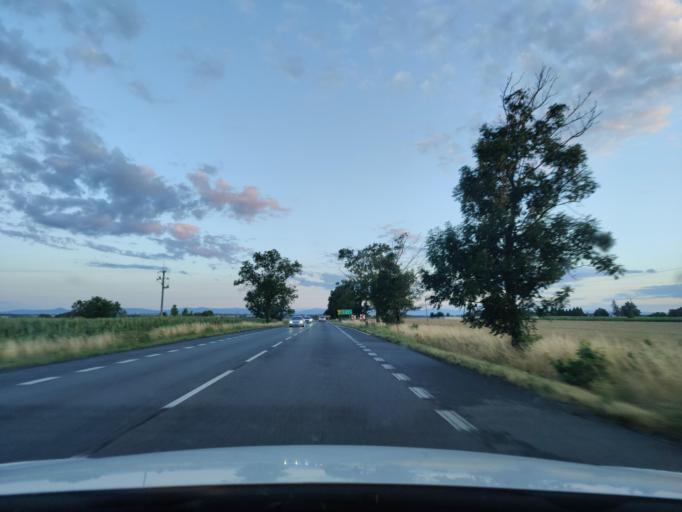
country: PL
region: Opole Voivodeship
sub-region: Powiat nyski
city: Pakoslawice
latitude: 50.5510
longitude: 17.3753
